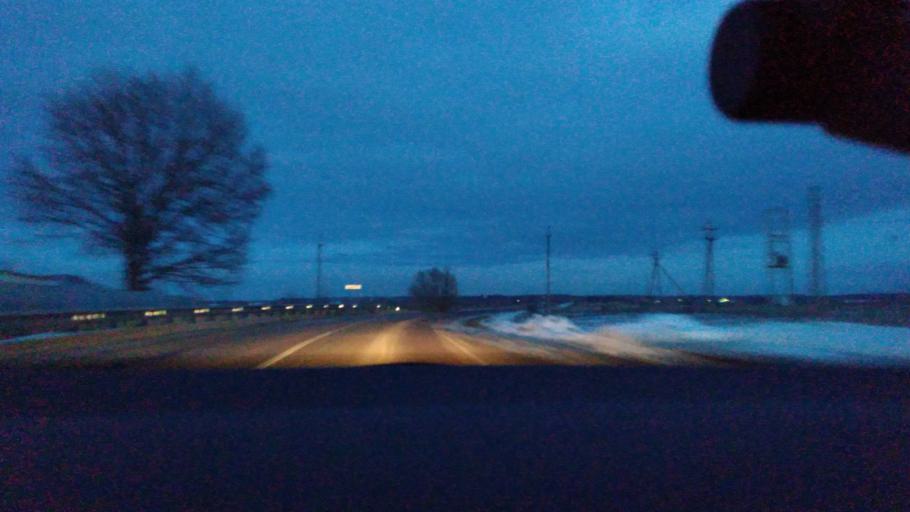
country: RU
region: Moskovskaya
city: Krasnaya Poyma
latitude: 55.1680
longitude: 39.1810
